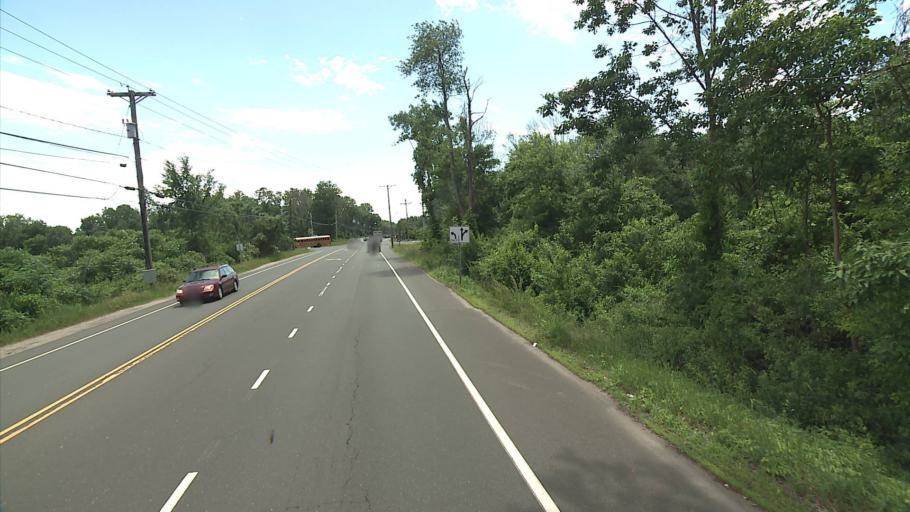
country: US
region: Connecticut
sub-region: Litchfield County
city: Oakville
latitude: 41.5567
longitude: -73.0929
